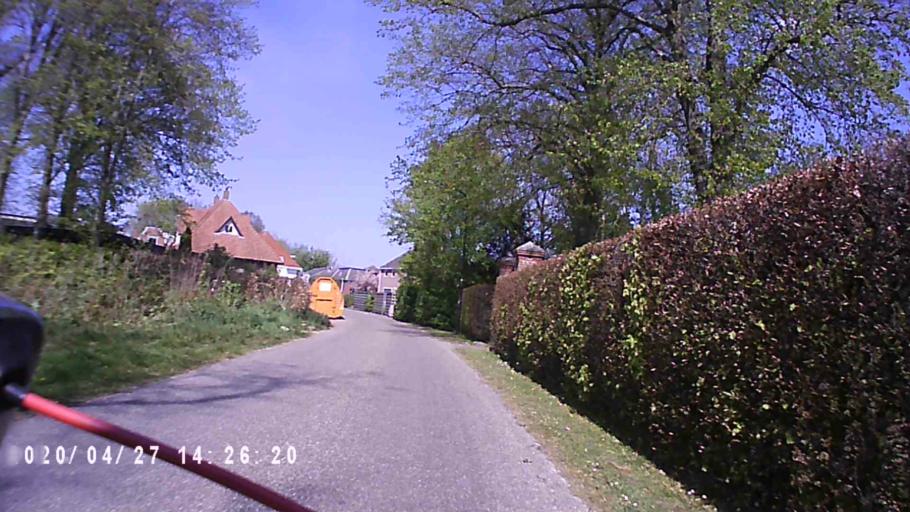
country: NL
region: Groningen
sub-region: Gemeente De Marne
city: Ulrum
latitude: 53.3867
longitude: 6.3951
